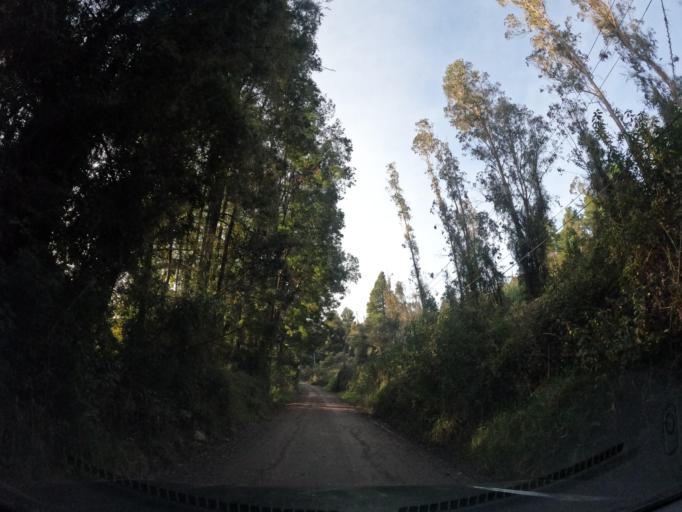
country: CL
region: Biobio
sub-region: Provincia de Concepcion
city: Chiguayante
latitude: -36.8708
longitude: -72.9951
